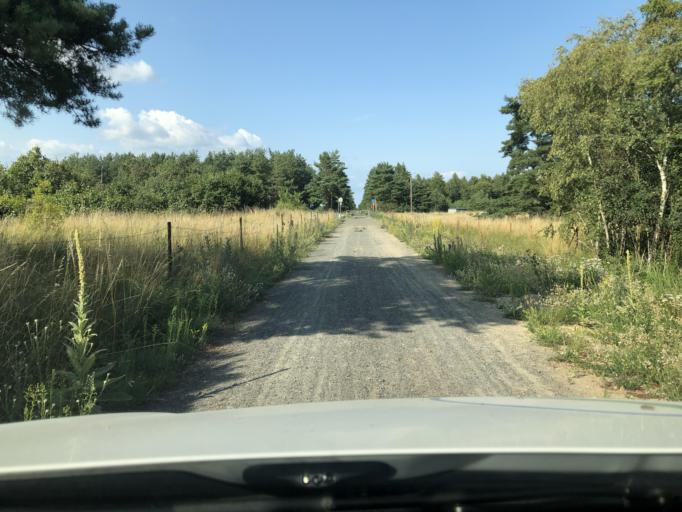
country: SE
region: Skane
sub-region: Kristianstads Kommun
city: Norra Asum
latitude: 55.9326
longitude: 14.1351
